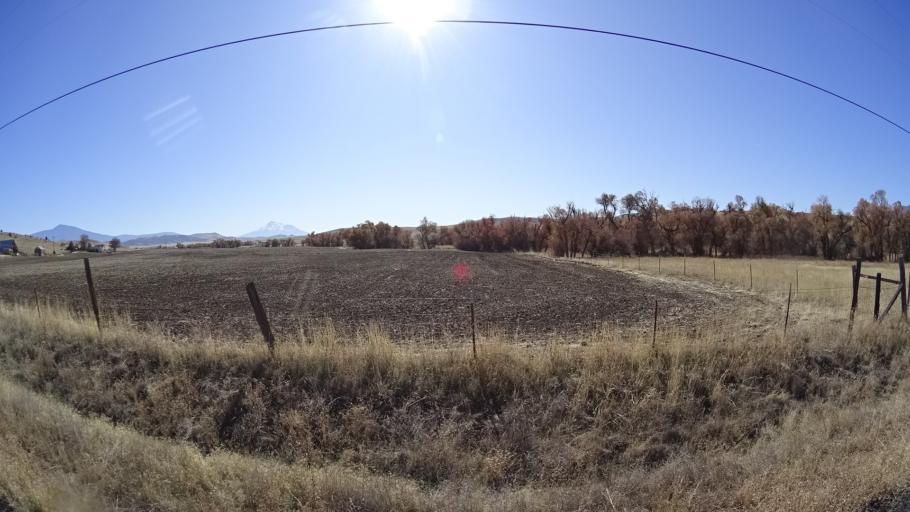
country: US
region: California
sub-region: Siskiyou County
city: Montague
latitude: 41.8480
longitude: -122.4546
